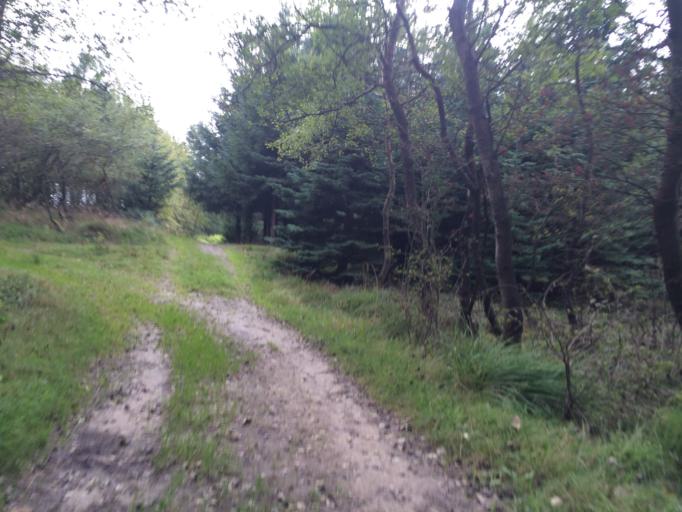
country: DK
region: Central Jutland
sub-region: Holstebro Kommune
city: Ulfborg
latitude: 56.2365
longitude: 8.4144
